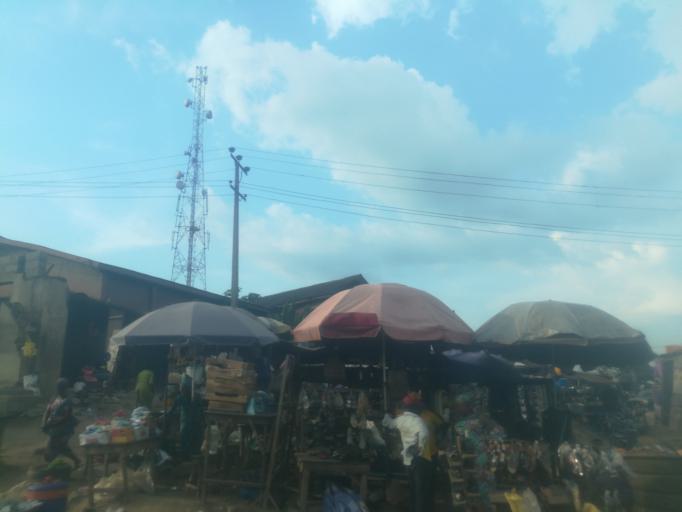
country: NG
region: Ogun
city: Abeokuta
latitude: 7.1585
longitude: 3.3253
